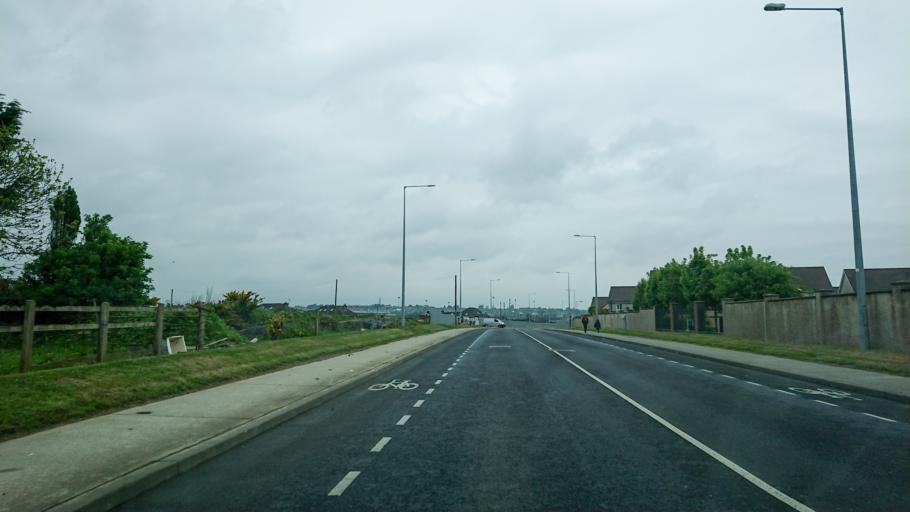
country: IE
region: Munster
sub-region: Waterford
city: Waterford
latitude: 52.2384
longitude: -7.1377
